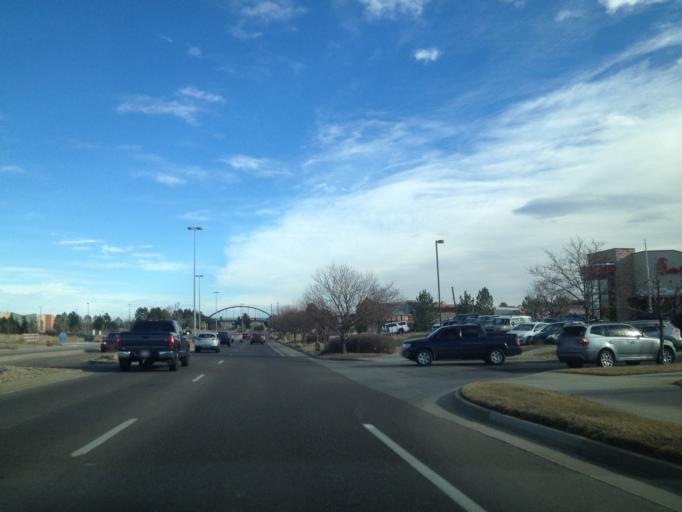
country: US
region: Colorado
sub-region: Boulder County
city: Superior
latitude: 39.9287
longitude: -105.1401
